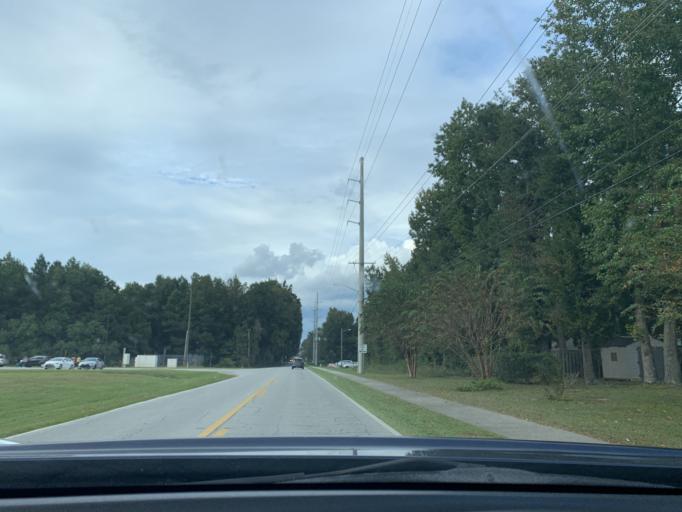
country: US
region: Georgia
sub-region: Chatham County
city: Pooler
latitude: 32.0942
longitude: -81.2565
